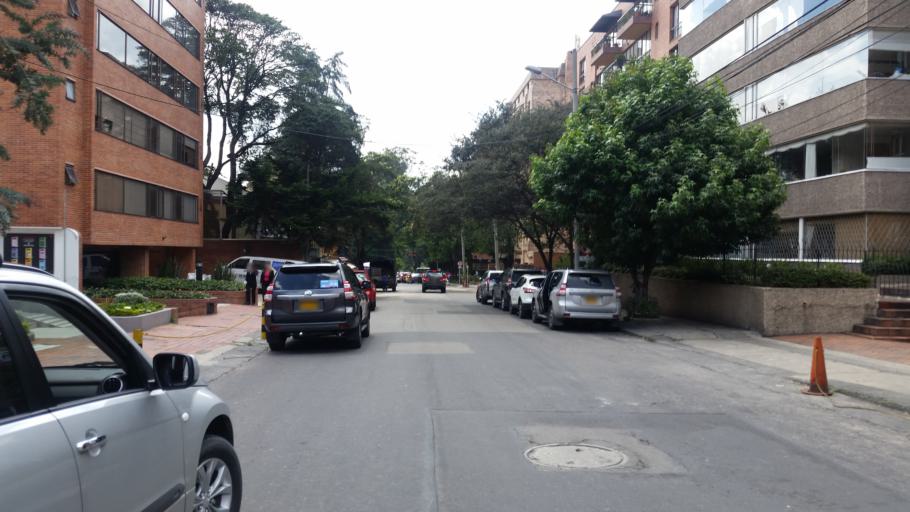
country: CO
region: Bogota D.C.
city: Barrio San Luis
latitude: 4.6521
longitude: -74.0553
